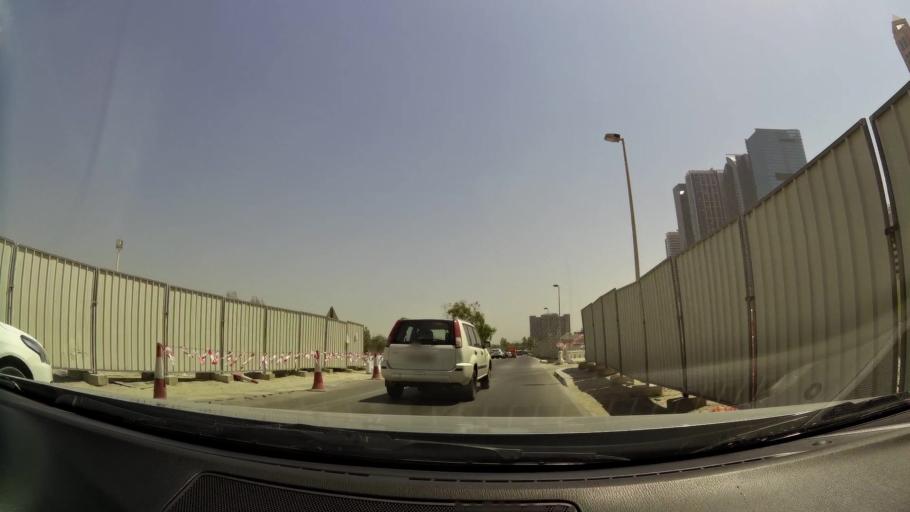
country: AE
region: Ash Shariqah
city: Sharjah
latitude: 25.2270
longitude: 55.2814
